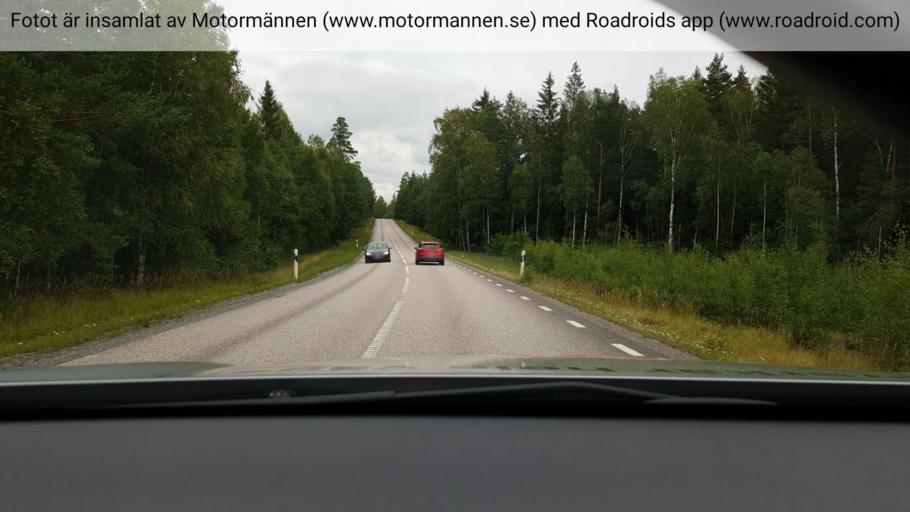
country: SE
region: Soedermanland
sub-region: Strangnas Kommun
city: Akers Styckebruk
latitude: 59.2254
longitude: 16.9202
